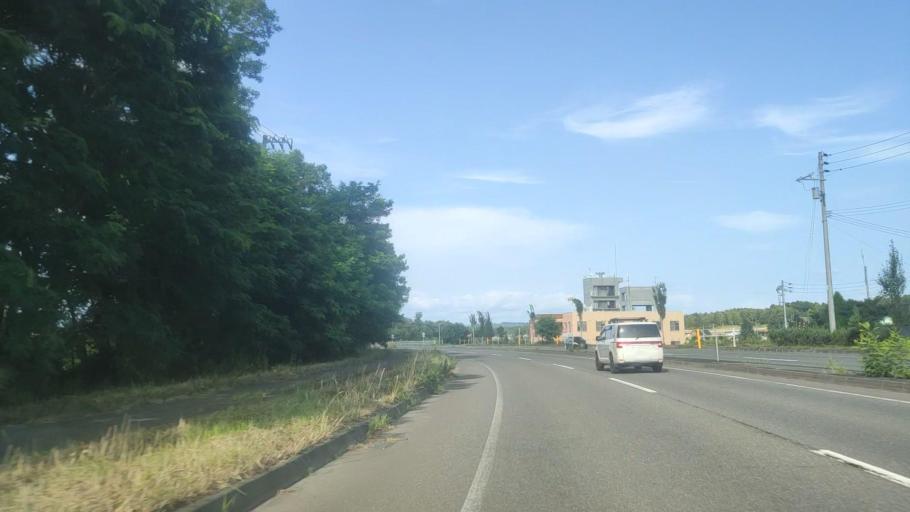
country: JP
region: Hokkaido
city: Chitose
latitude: 42.7699
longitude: 141.8230
